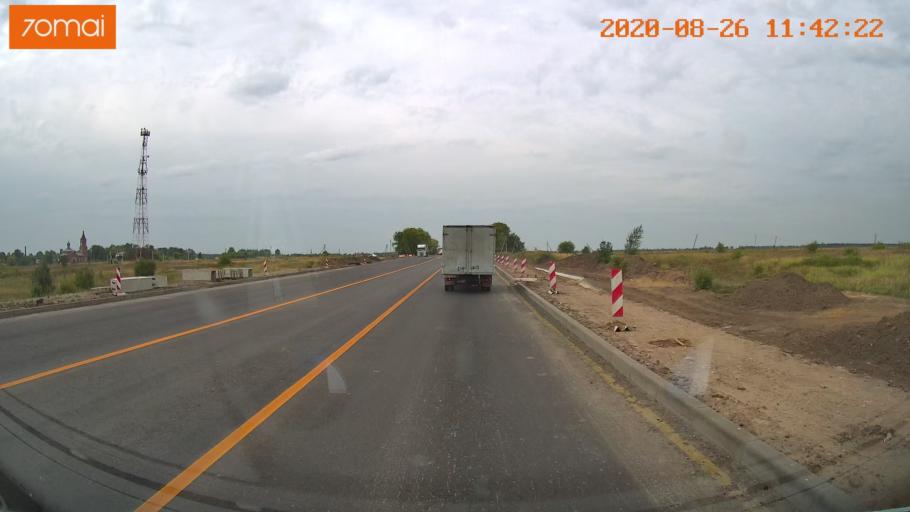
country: RU
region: Rjazan
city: Shilovo
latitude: 54.2973
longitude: 40.6946
